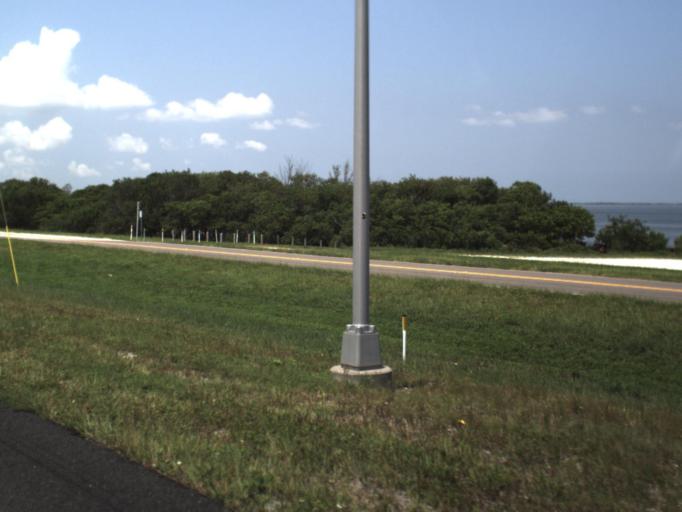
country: US
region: Florida
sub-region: Pinellas County
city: Gandy
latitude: 27.8786
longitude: -82.5854
